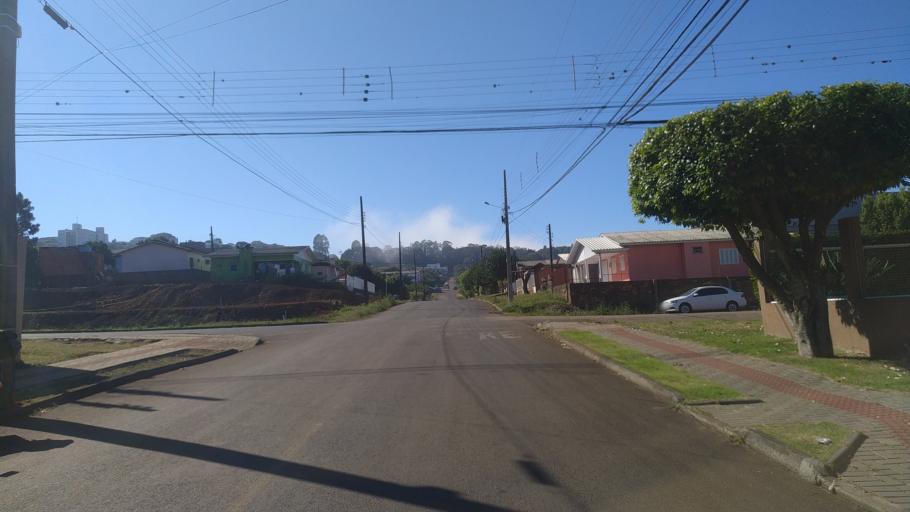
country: BR
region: Santa Catarina
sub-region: Chapeco
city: Chapeco
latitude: -27.1143
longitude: -52.5993
